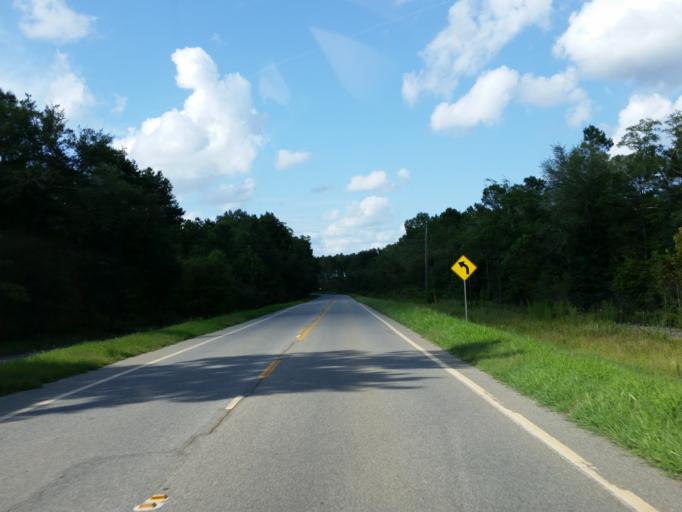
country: US
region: Georgia
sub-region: Lee County
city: Leesburg
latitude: 31.8627
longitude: -84.0736
